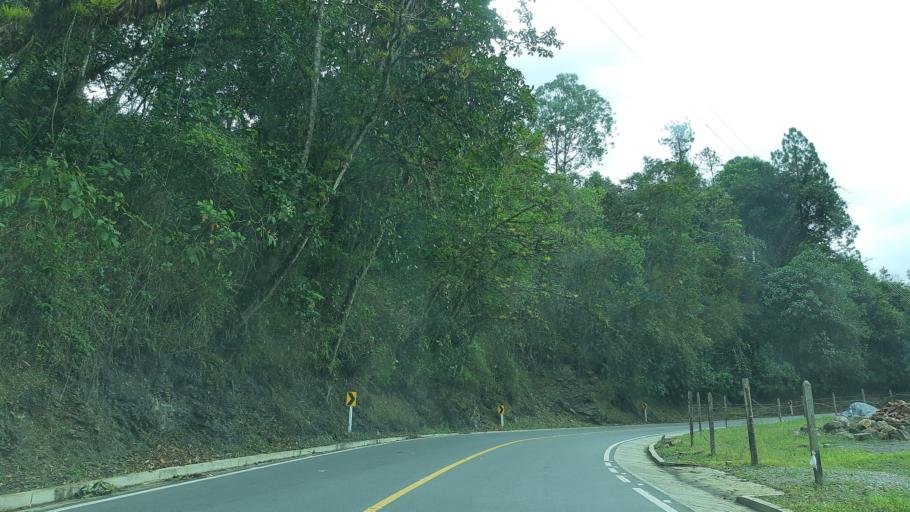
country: CO
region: Boyaca
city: Chivor
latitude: 4.9473
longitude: -73.3043
